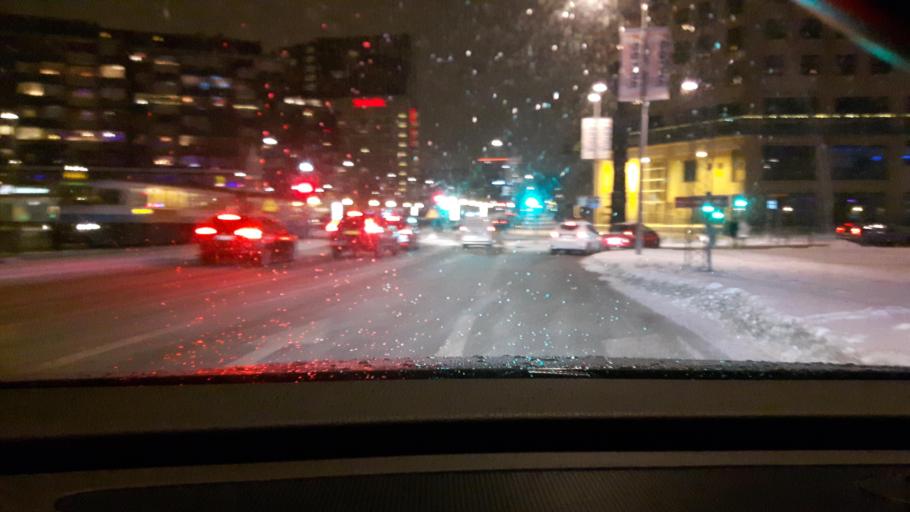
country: SE
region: Vaestra Goetaland
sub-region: Goteborg
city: Goeteborg
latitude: 57.6996
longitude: 11.9866
